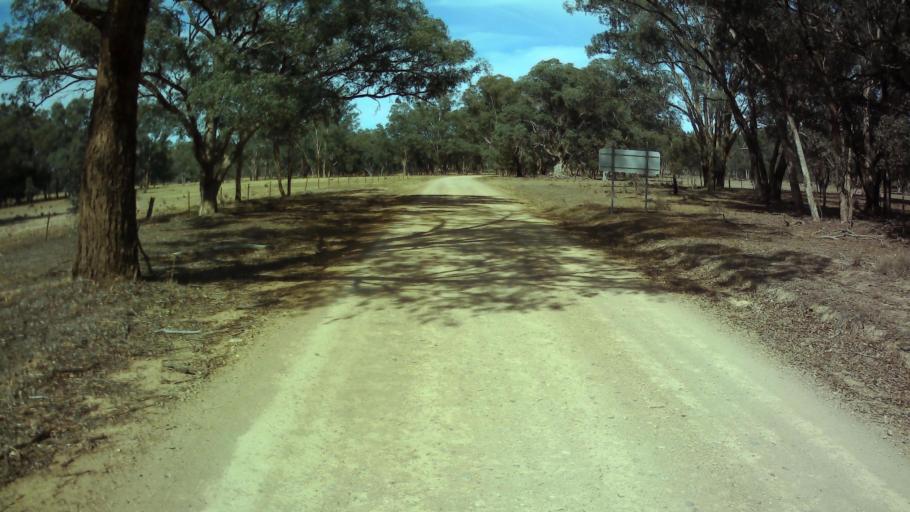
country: AU
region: New South Wales
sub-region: Weddin
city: Grenfell
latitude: -33.6844
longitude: 148.2792
